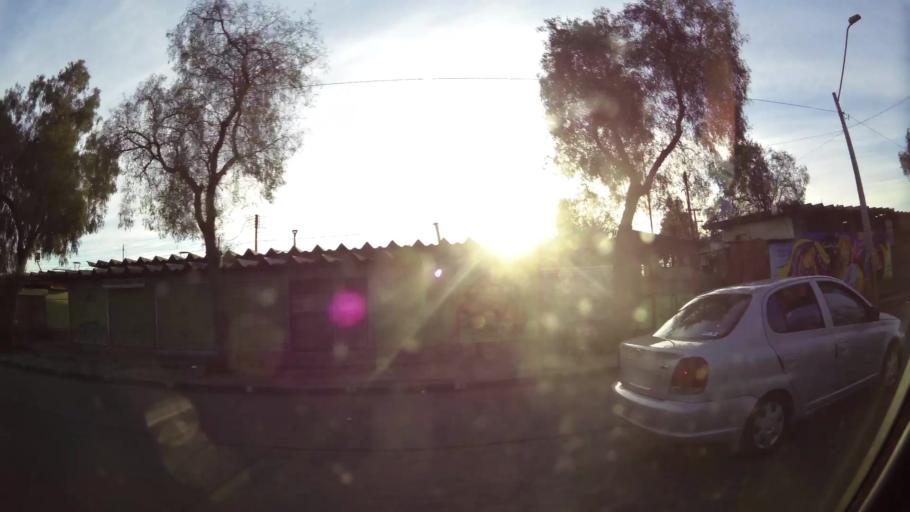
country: CL
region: Santiago Metropolitan
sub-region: Provincia de Santiago
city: Lo Prado
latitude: -33.4472
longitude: -70.7227
